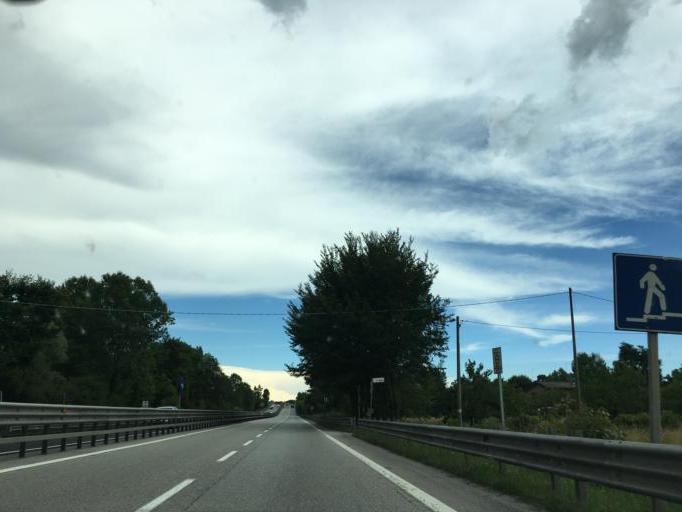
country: IT
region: Veneto
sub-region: Provincia di Treviso
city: Mogliano Veneto
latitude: 45.5138
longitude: 12.2507
